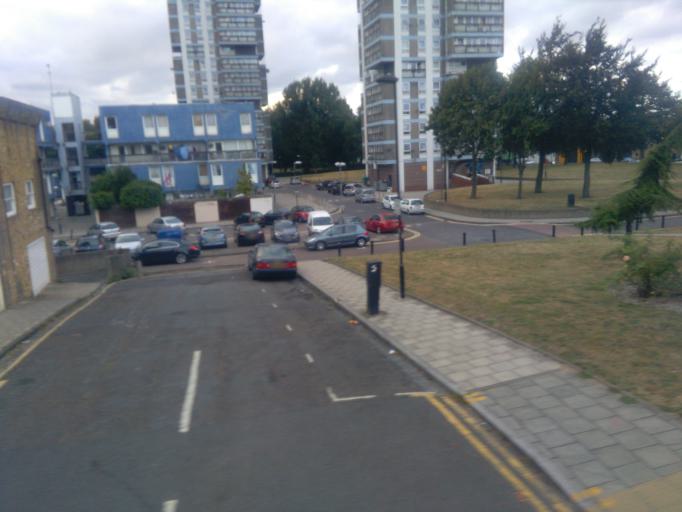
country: GB
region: England
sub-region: Greater London
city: Battersea
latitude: 51.4701
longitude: -0.1402
